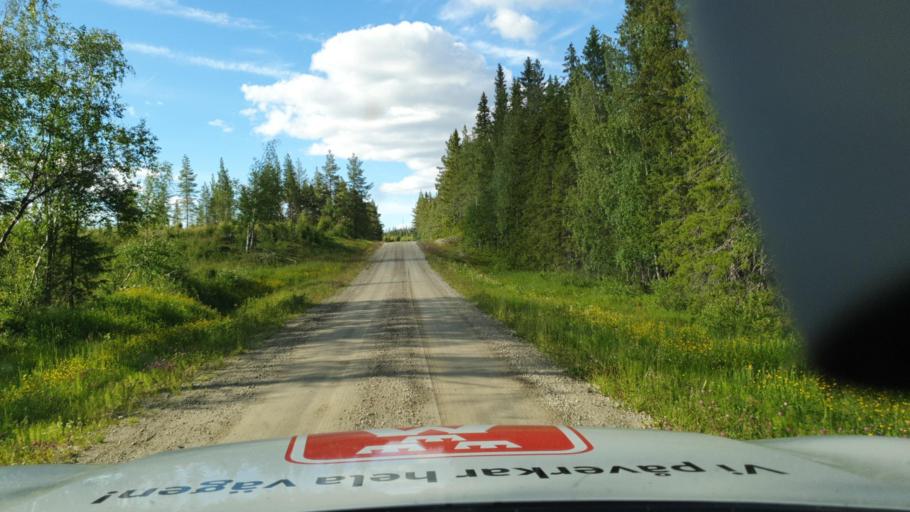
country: SE
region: Vaesterbotten
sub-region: Lycksele Kommun
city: Lycksele
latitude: 64.4790
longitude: 18.2859
